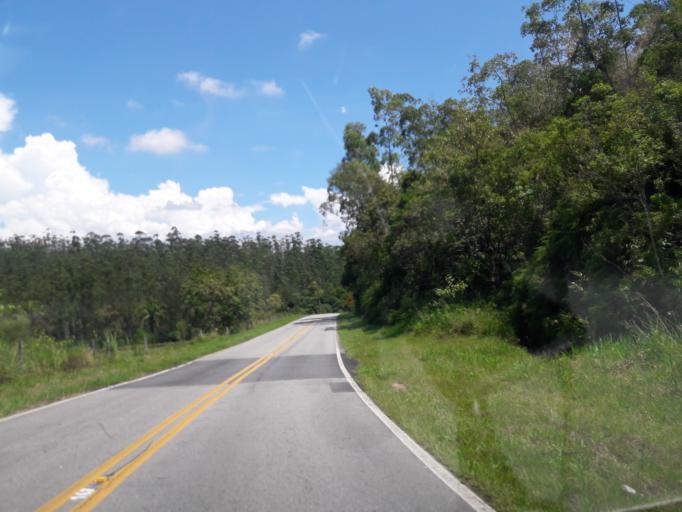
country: BR
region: Parana
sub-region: Antonina
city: Antonina
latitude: -25.5260
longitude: -48.7744
